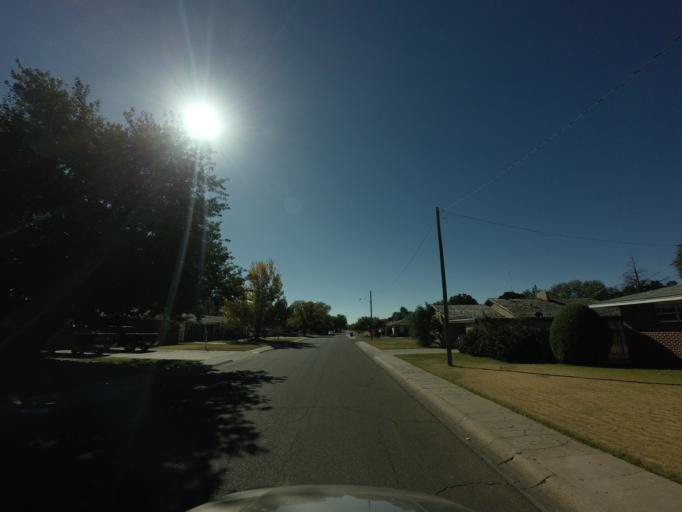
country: US
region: New Mexico
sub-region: Curry County
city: Clovis
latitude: 34.4237
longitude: -103.2026
